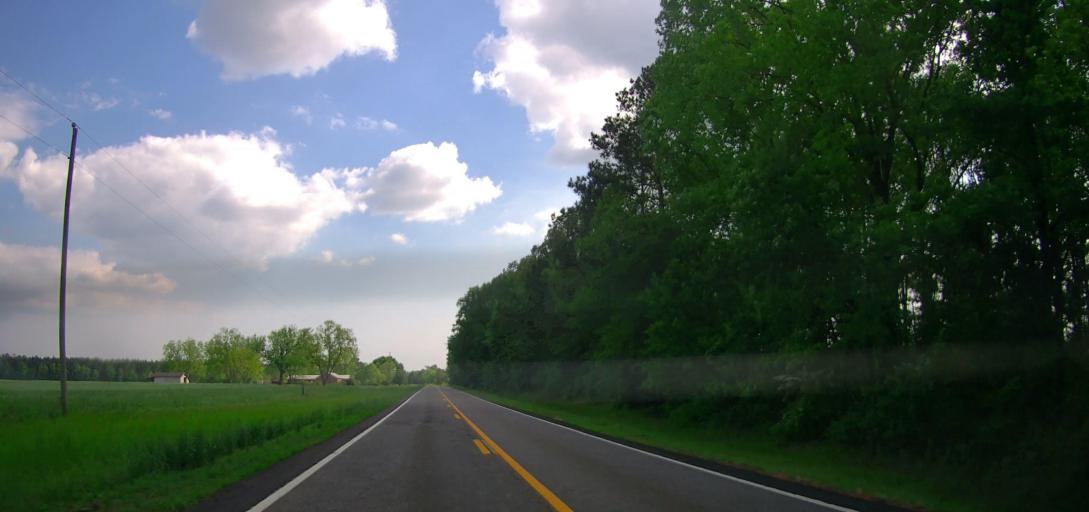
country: US
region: Georgia
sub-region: Laurens County
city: East Dublin
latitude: 32.6538
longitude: -82.8962
